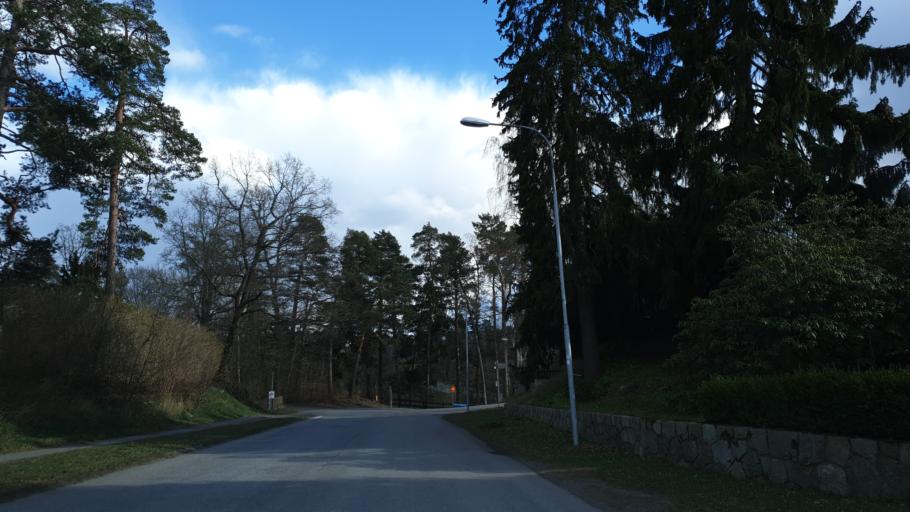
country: SE
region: Stockholm
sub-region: Lidingo
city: Lidingoe
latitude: 59.3722
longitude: 18.1268
